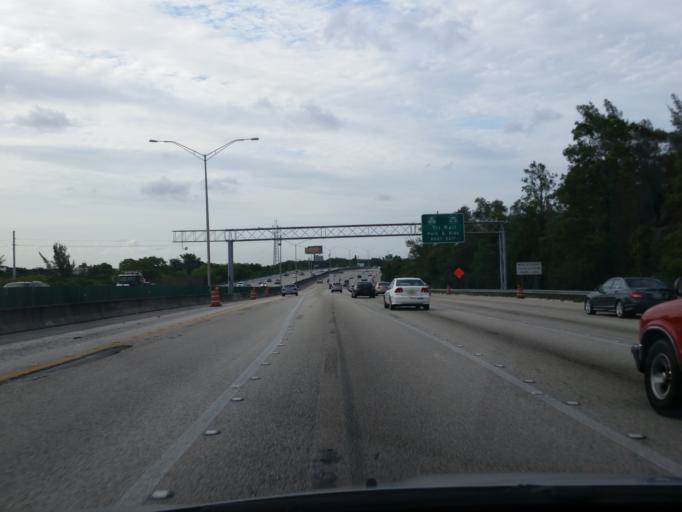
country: US
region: Florida
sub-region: Broward County
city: Hollywood
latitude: 26.0199
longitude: -80.1671
